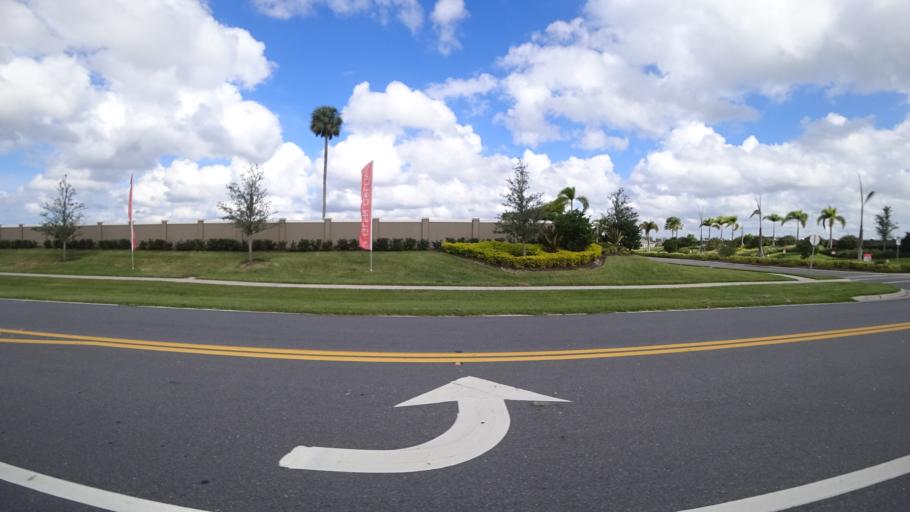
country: US
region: Florida
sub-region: Manatee County
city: Samoset
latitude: 27.4768
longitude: -82.5329
